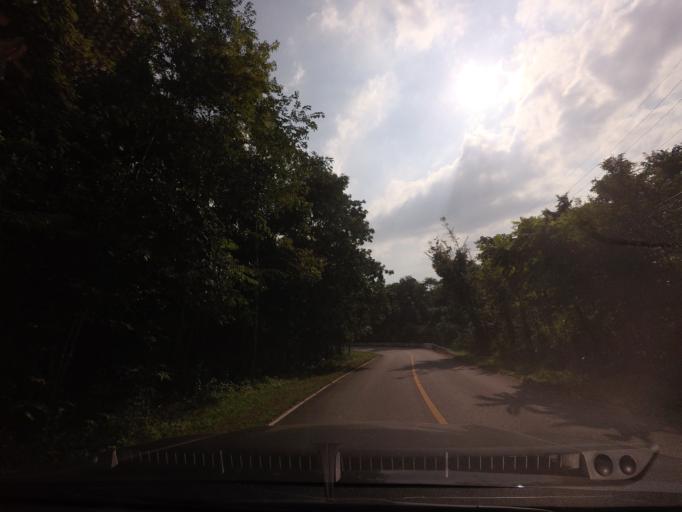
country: TH
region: Phitsanulok
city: Nakhon Thai
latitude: 17.0185
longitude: 100.9585
